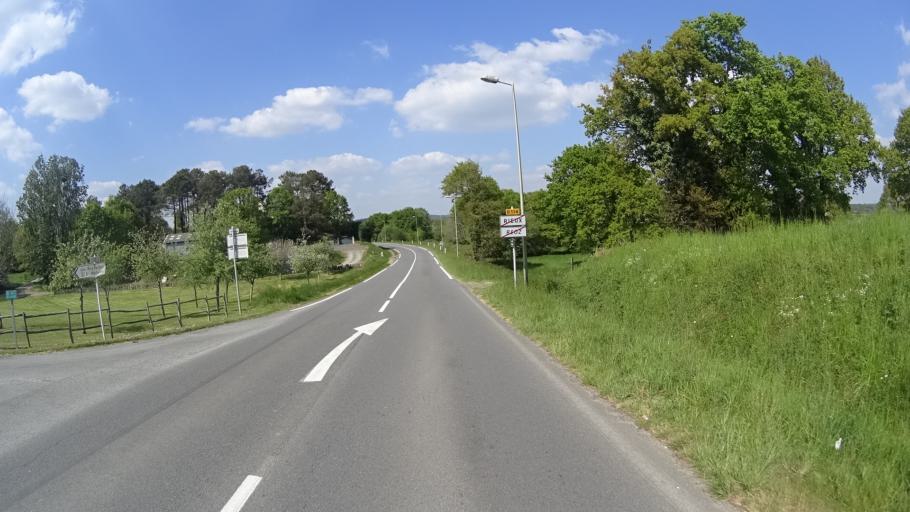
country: FR
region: Brittany
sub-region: Departement du Morbihan
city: Rieux
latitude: 47.5992
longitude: -2.1037
